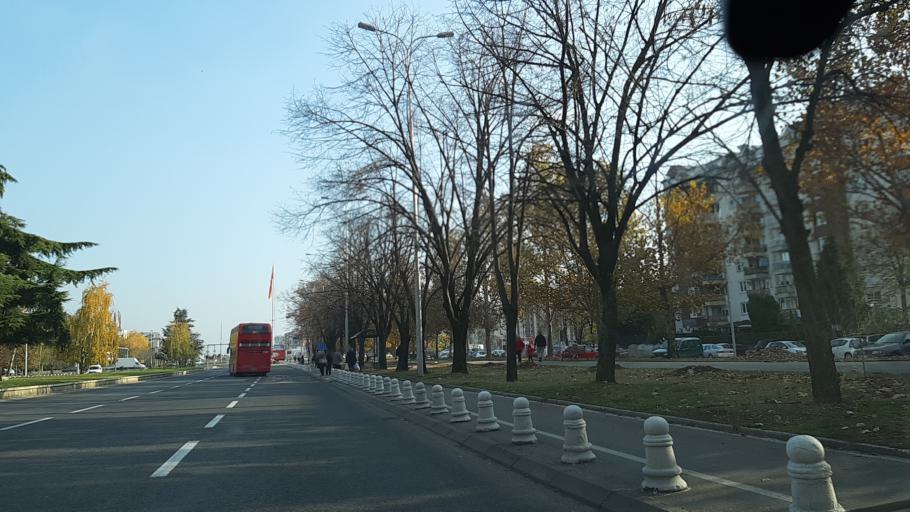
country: MK
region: Kisela Voda
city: Usje
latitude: 41.9837
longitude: 21.4690
